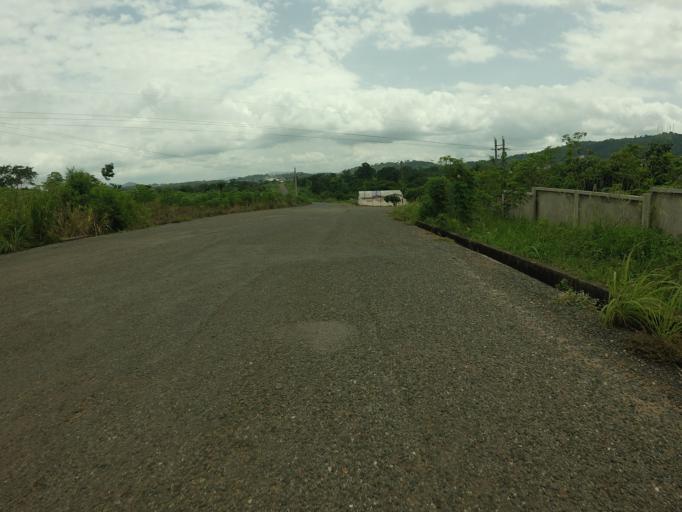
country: GH
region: Volta
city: Ho
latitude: 6.5936
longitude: 0.4603
